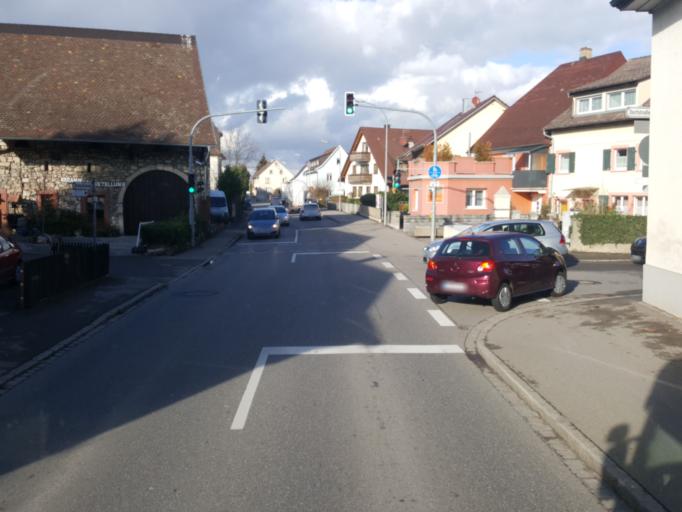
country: DE
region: Baden-Wuerttemberg
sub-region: Freiburg Region
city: Eimeldingen
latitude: 47.6320
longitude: 7.5952
